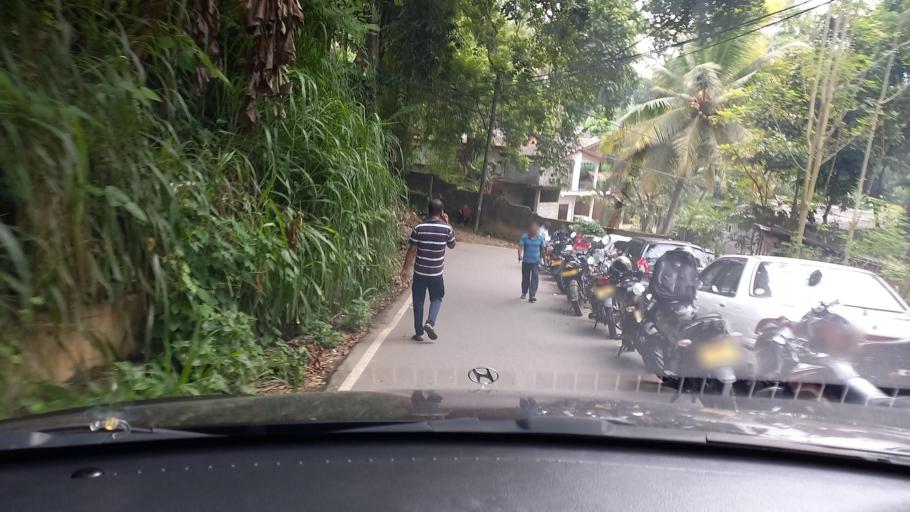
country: LK
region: Central
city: Kadugannawa
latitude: 7.2553
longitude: 80.3509
